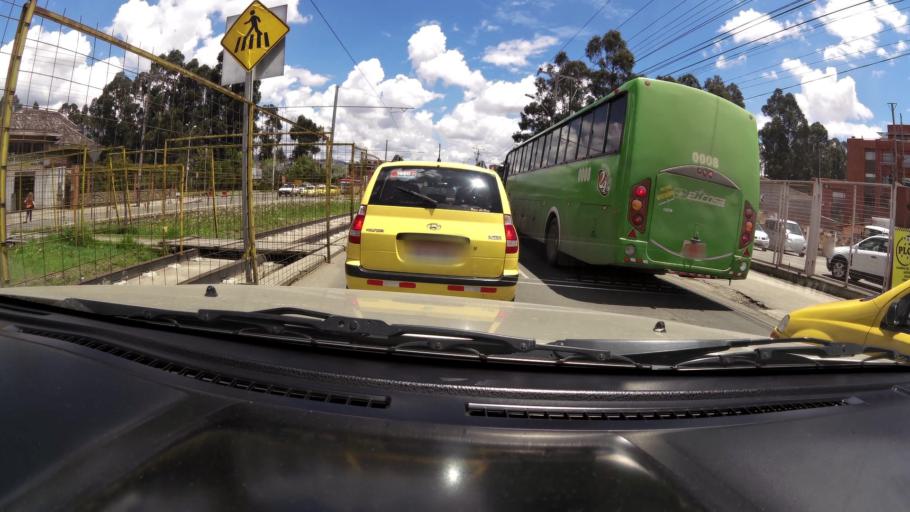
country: EC
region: Azuay
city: Cuenca
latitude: -2.9074
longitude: -79.0337
